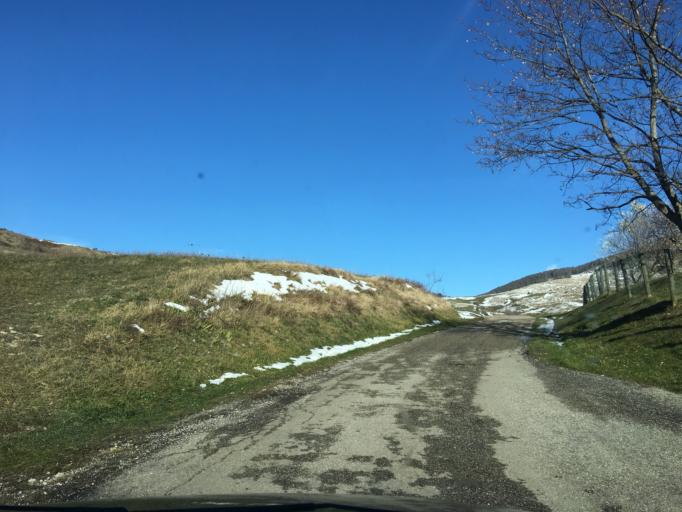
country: IT
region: Molise
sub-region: Provincia di Isernia
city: Agnone
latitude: 41.8474
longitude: 14.3524
